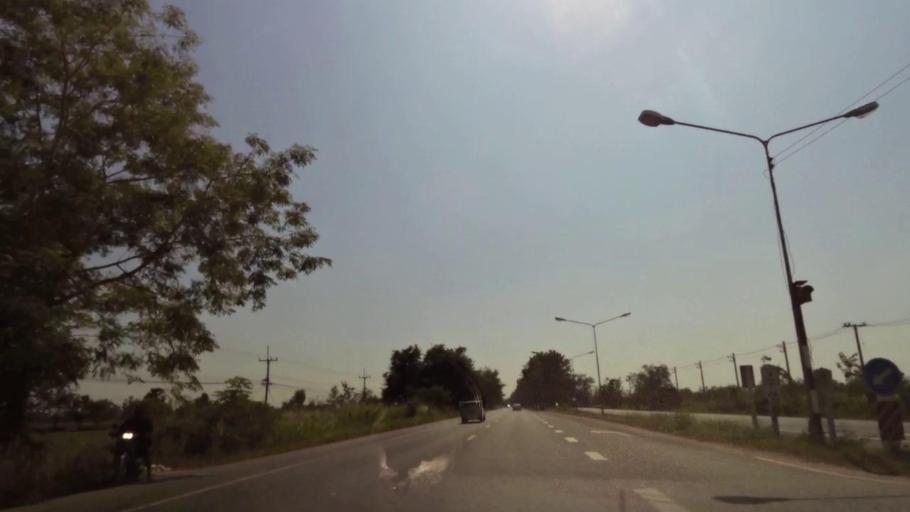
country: TH
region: Nakhon Sawan
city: Kao Liao
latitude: 15.9296
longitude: 100.1124
